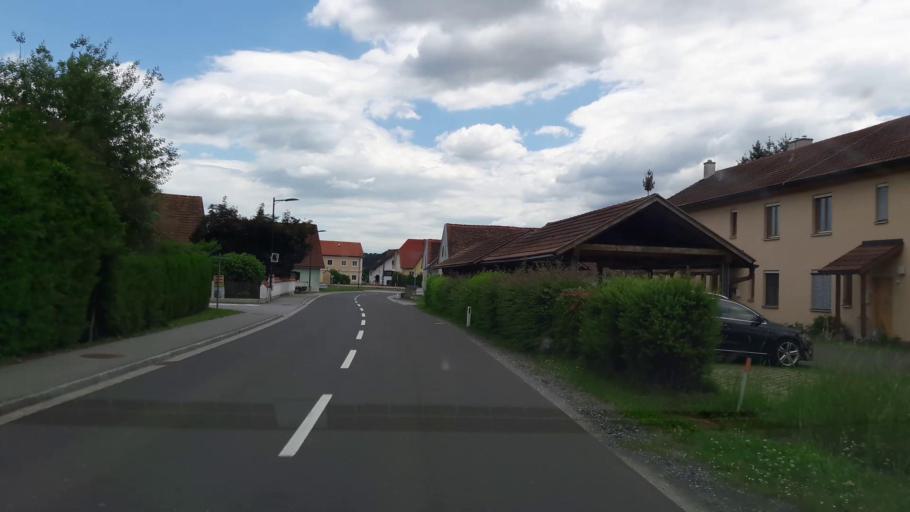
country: AT
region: Styria
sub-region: Politischer Bezirk Hartberg-Fuerstenfeld
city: UEbersbach
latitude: 47.0211
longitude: 16.0512
